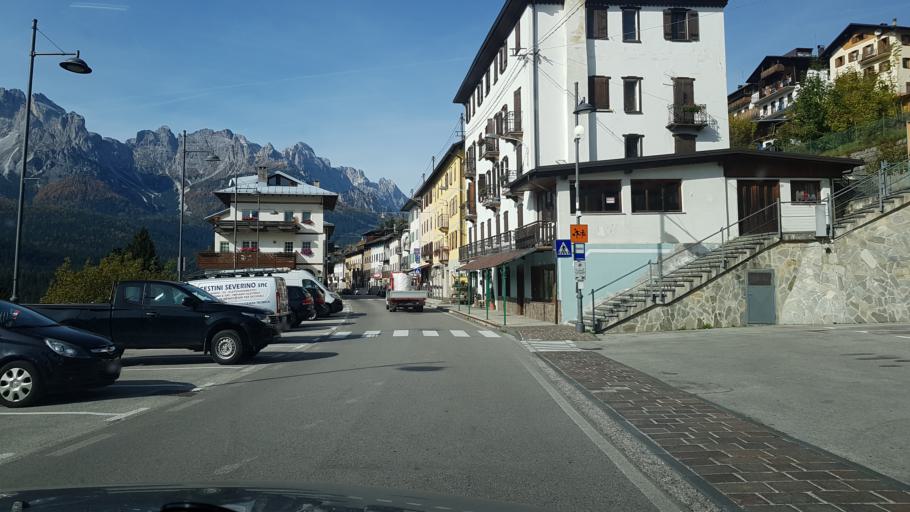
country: IT
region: Veneto
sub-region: Provincia di Belluno
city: Candide
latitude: 46.5892
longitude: 12.5140
